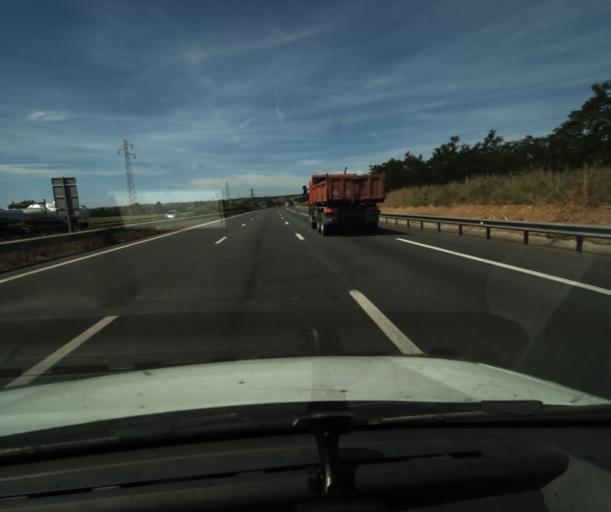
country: FR
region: Midi-Pyrenees
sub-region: Departement de la Haute-Garonne
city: Saint-Sauveur
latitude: 43.7537
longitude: 1.3860
